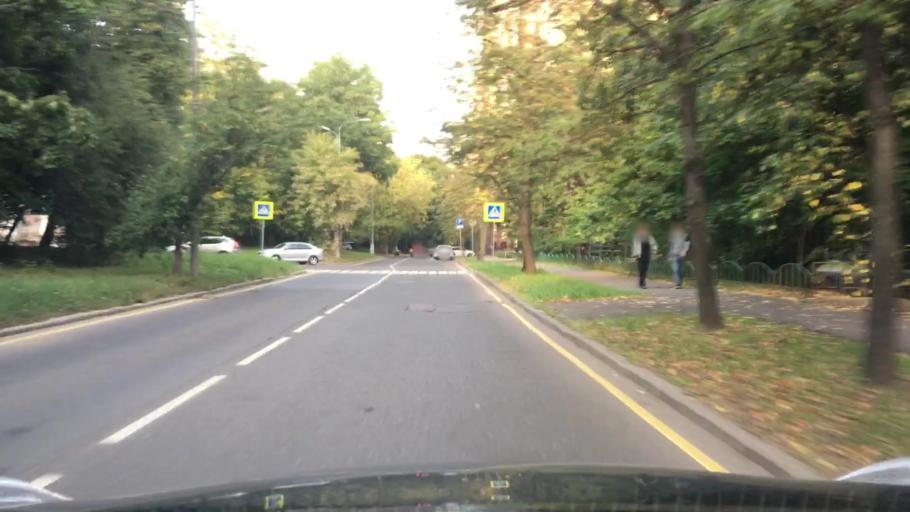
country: RU
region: Moscow
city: Davydkovo
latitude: 55.7354
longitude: 37.4518
